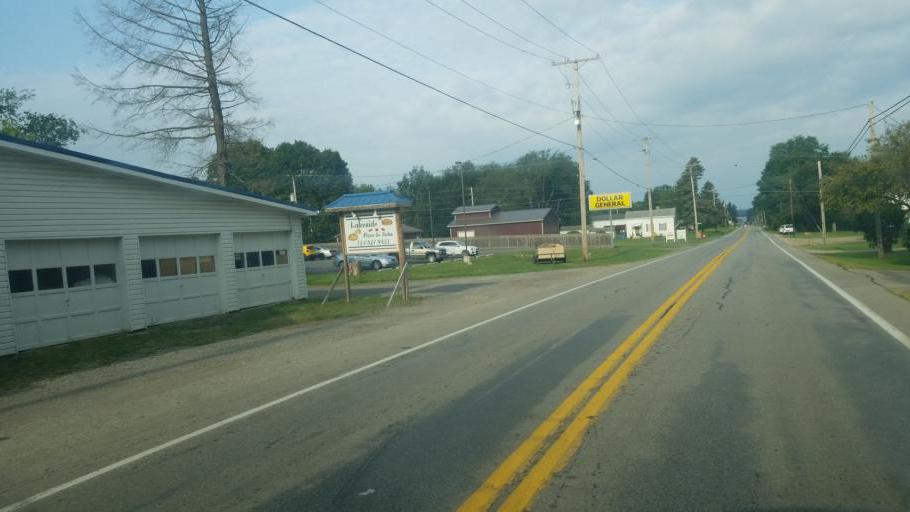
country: US
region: Pennsylvania
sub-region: Crawford County
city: Pymatuning Central
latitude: 41.6062
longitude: -80.4883
